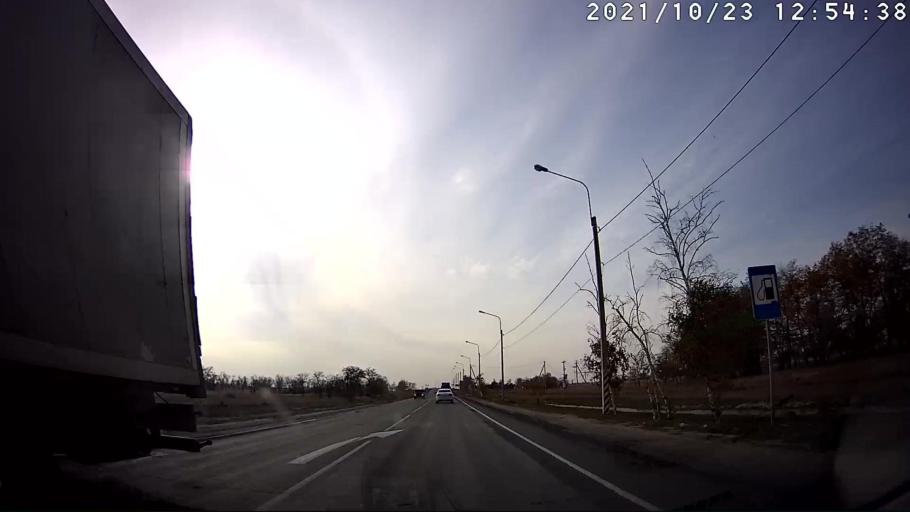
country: RU
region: Volgograd
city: Dubovka
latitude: 49.0556
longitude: 44.7988
